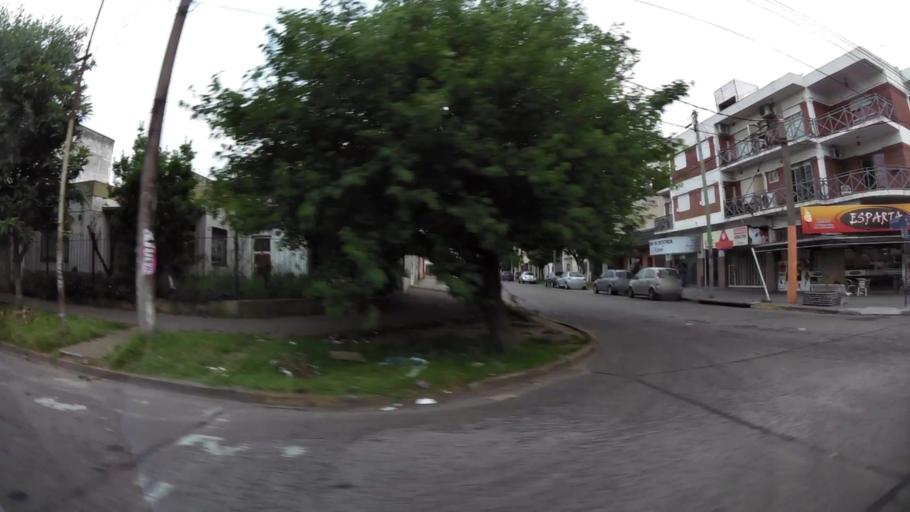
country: AR
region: Buenos Aires
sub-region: Partido de Moron
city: Moron
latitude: -34.6566
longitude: -58.5897
